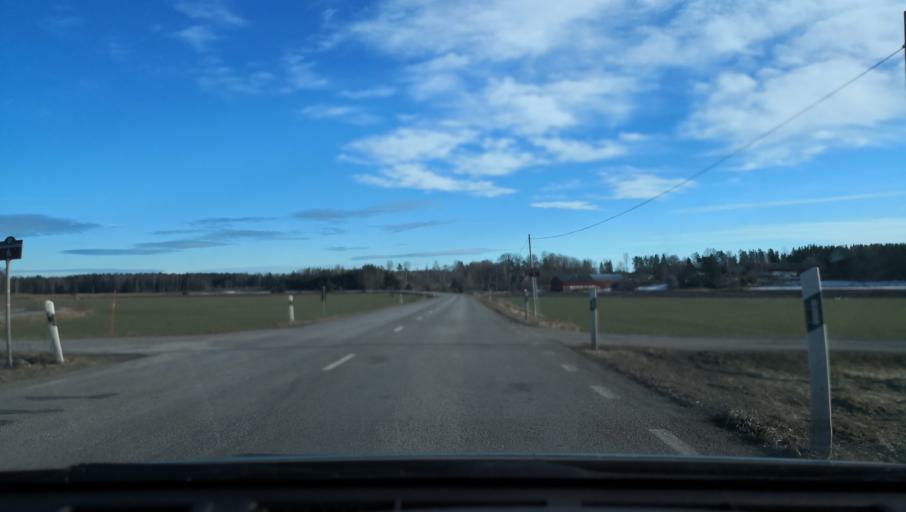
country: SE
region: Uppsala
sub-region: Osthammars Kommun
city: Osterbybruk
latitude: 60.1649
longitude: 17.9777
